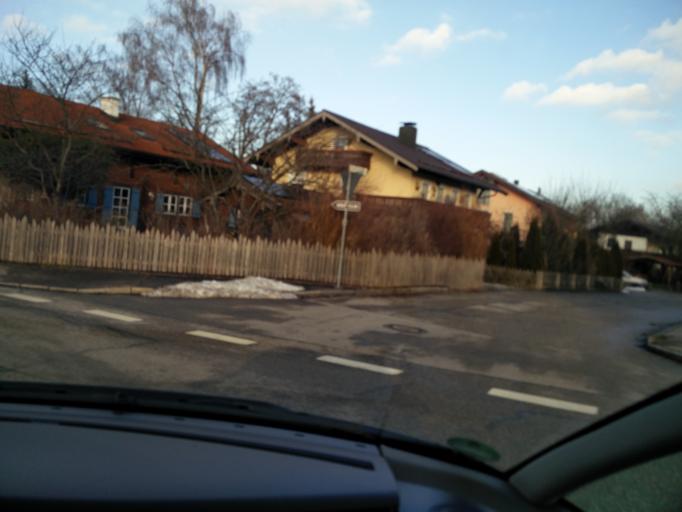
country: DE
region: Bavaria
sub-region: Upper Bavaria
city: Hoslwang
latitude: 47.9550
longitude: 12.3292
